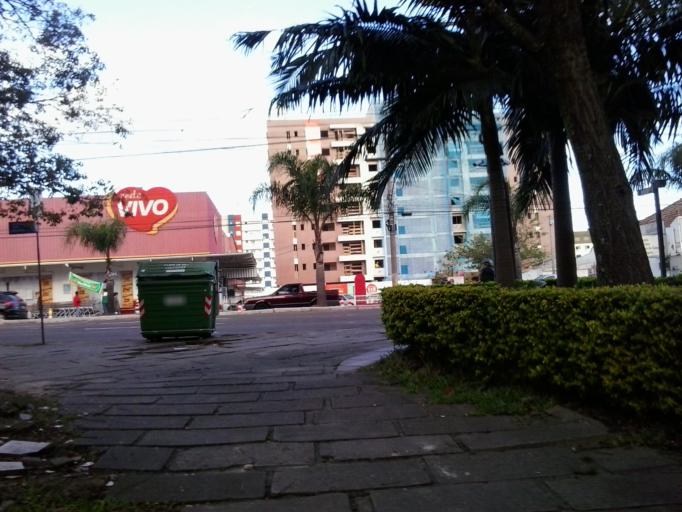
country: BR
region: Rio Grande do Sul
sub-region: Santa Maria
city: Santa Maria
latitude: -29.6899
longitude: -53.8003
